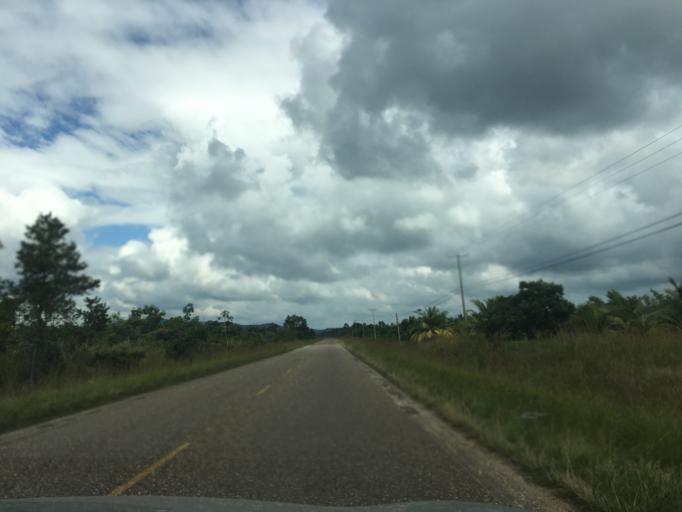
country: BZ
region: Stann Creek
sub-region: Dangriga
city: Dangriga
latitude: 16.8985
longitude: -88.3400
